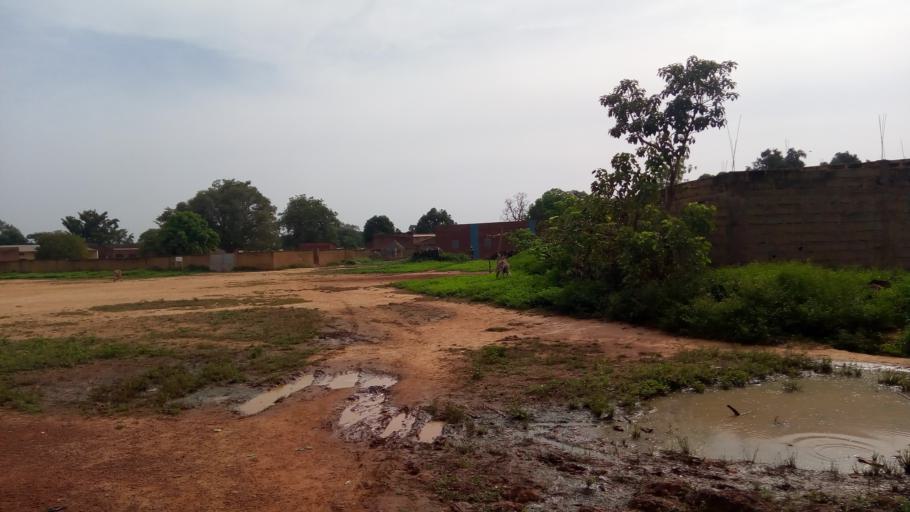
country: ML
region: Koulikoro
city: Kangaba
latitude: 11.6886
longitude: -8.6956
